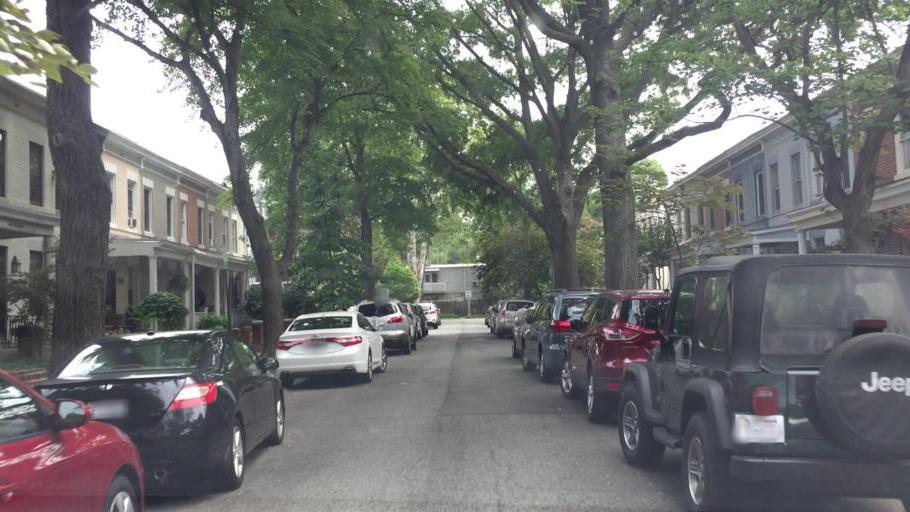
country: US
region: Washington, D.C.
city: Washington, D.C.
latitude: 38.8868
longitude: -76.9894
